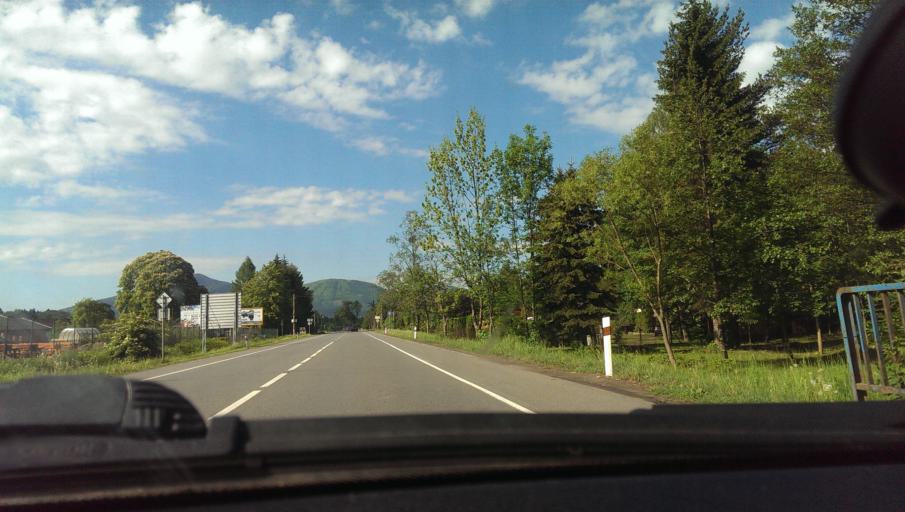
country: CZ
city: Frydlant nad Ostravici
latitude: 49.5678
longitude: 18.3558
